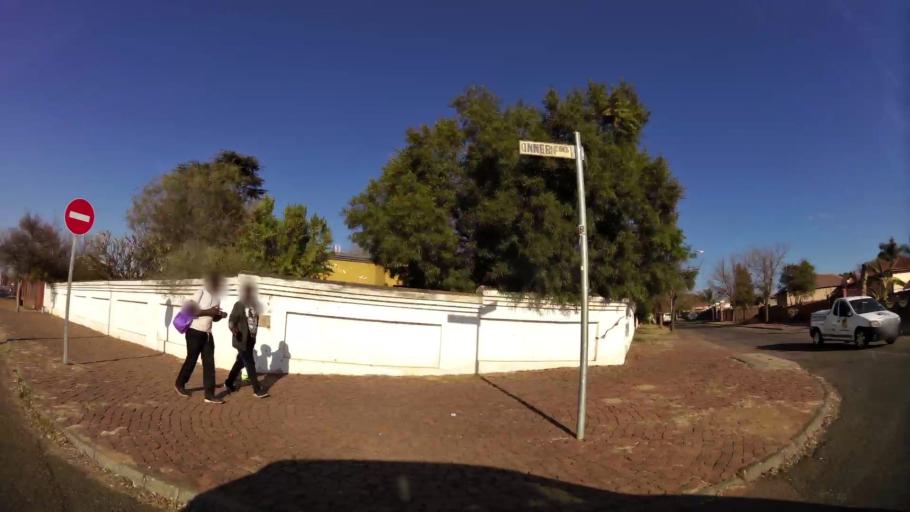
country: ZA
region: Gauteng
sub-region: City of Tshwane Metropolitan Municipality
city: Pretoria
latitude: -25.7545
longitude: 28.1250
